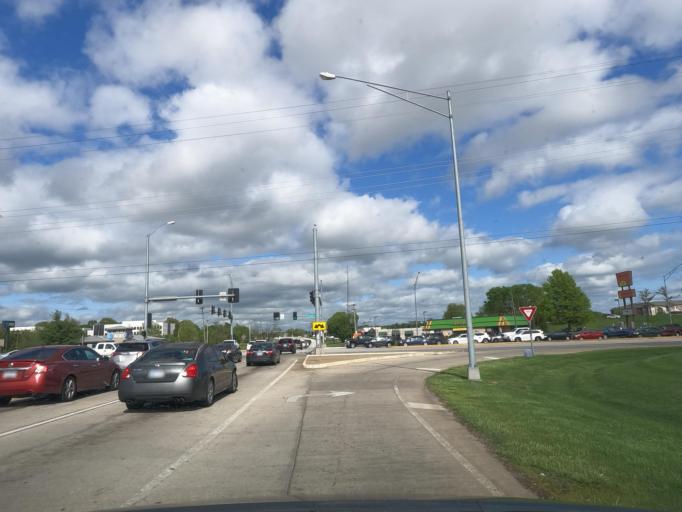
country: US
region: Missouri
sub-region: Greene County
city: Battlefield
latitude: 37.1381
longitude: -93.2969
